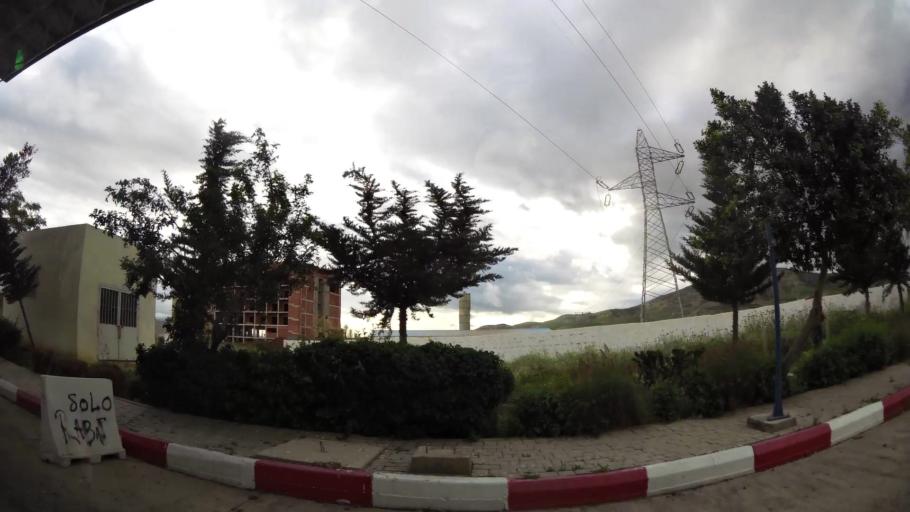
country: MA
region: Taza-Al Hoceima-Taounate
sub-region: Taza
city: Taza
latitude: 34.2680
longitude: -3.9548
